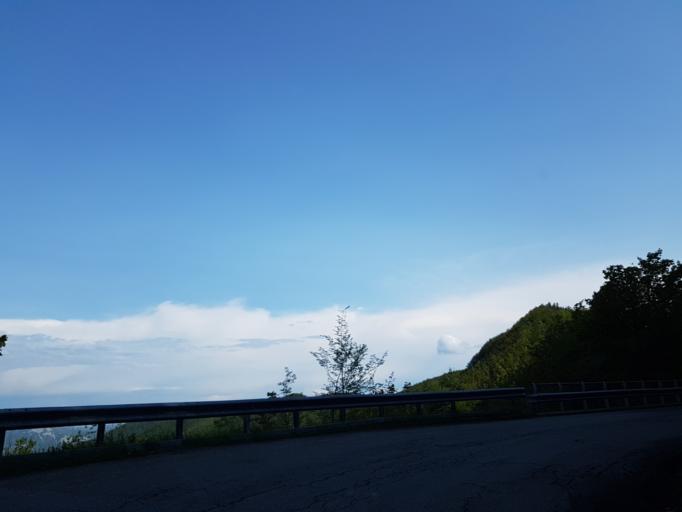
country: IT
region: Emilia-Romagna
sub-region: Forli-Cesena
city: San Piero in Bagno
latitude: 43.7992
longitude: 11.9142
